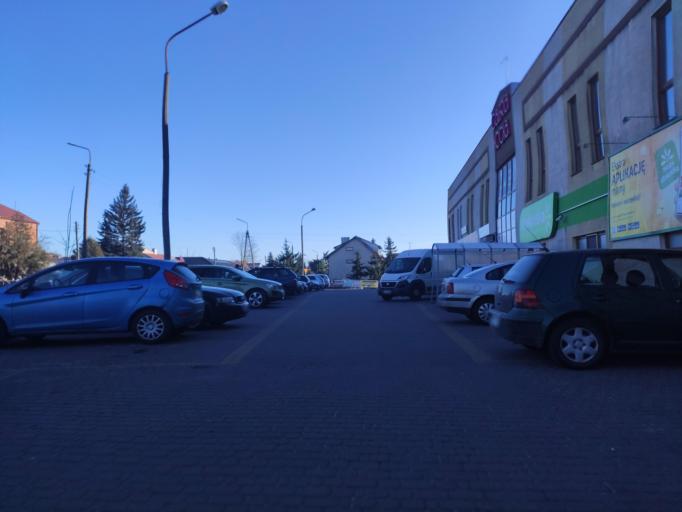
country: PL
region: Lublin Voivodeship
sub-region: Powiat lubartowski
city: Kock
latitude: 51.6419
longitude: 22.4475
